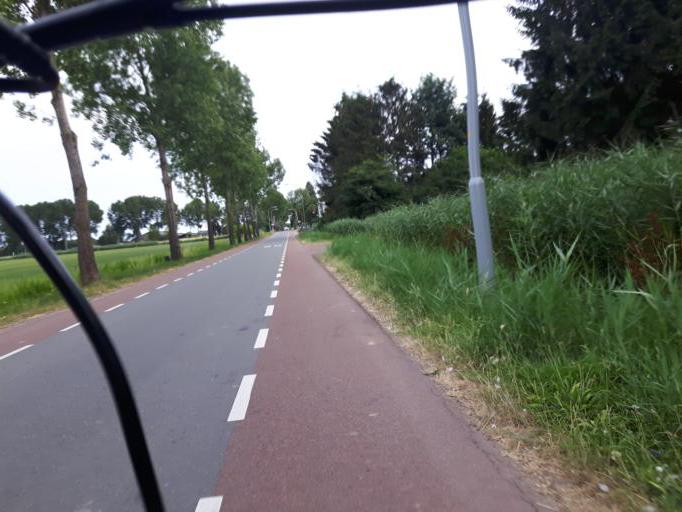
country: NL
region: Gelderland
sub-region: Gemeente Maasdriel
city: Heerewaarden
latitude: 51.8701
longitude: 5.3730
